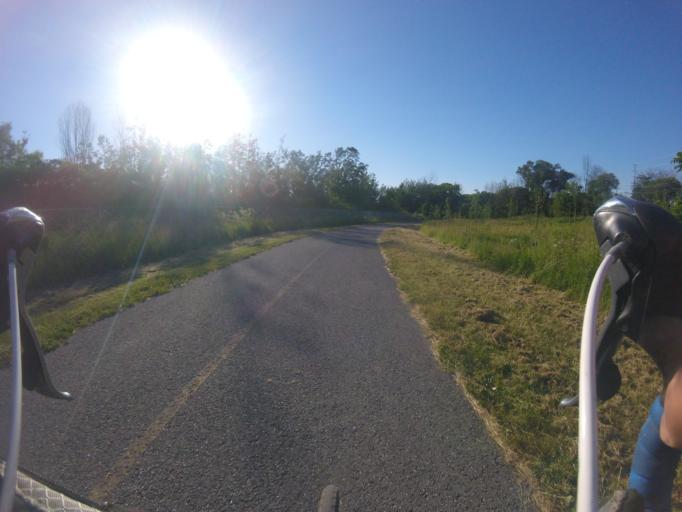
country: CA
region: Ontario
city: Bells Corners
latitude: 45.3344
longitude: -75.8100
